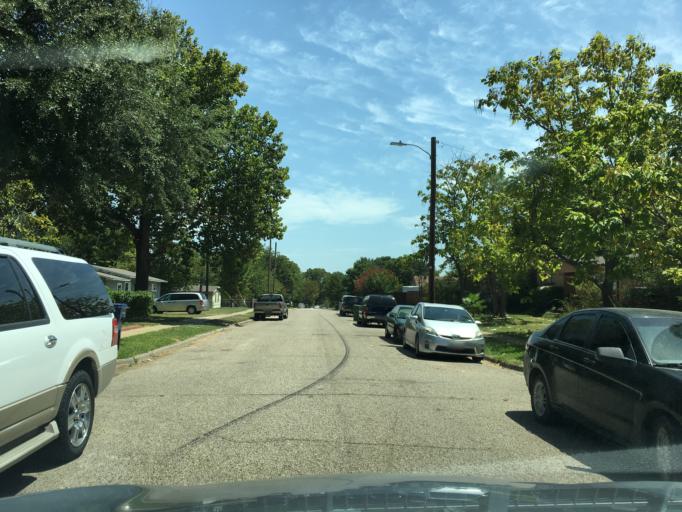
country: US
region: Texas
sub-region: Dallas County
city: Garland
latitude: 32.8951
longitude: -96.6273
